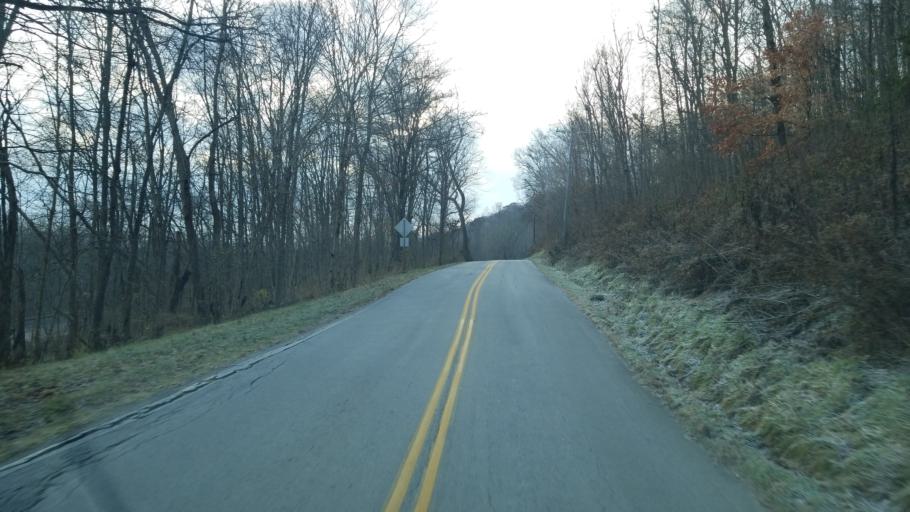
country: US
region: Ohio
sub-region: Ross County
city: Chillicothe
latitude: 39.2340
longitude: -82.8920
